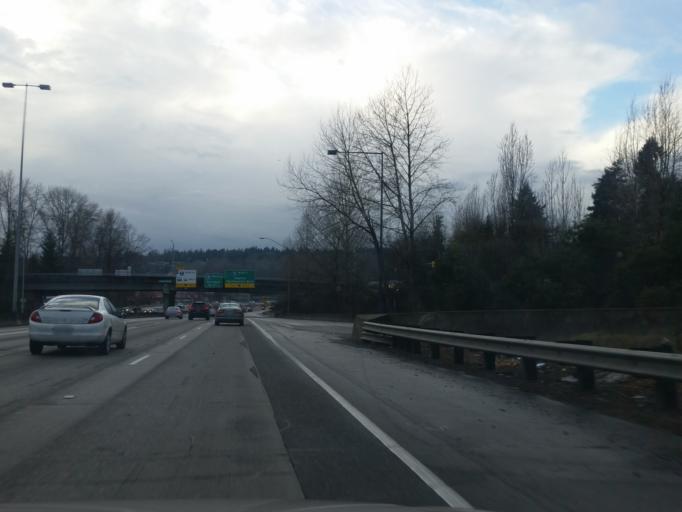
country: US
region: Washington
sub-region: King County
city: Tukwila
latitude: 47.4634
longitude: -122.2475
